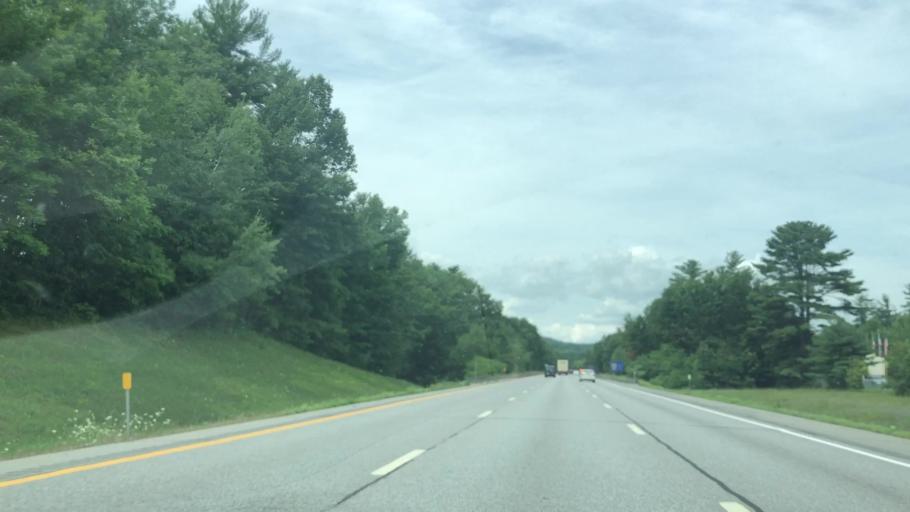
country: US
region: New York
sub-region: Warren County
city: Glens Falls North
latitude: 43.3507
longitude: -73.6973
